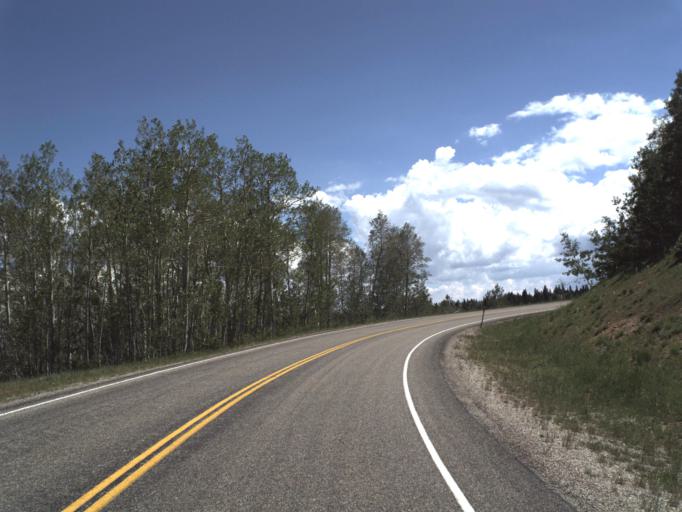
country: US
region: Utah
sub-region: Weber County
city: Wolf Creek
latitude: 41.4527
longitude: -111.5018
